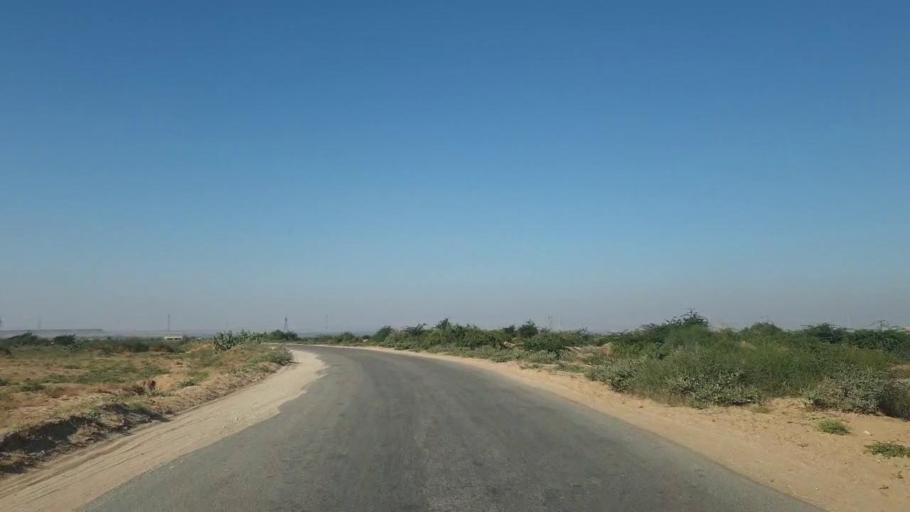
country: PK
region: Sindh
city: Gharo
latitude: 25.1662
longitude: 67.6621
